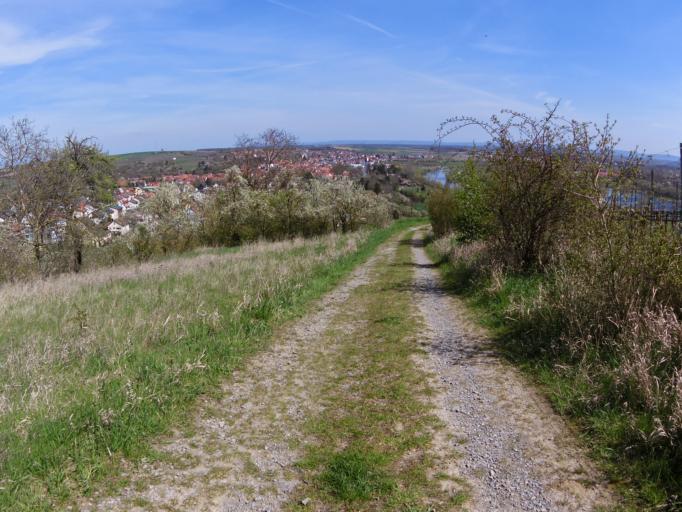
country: DE
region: Bavaria
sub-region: Regierungsbezirk Unterfranken
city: Mainstockheim
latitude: 49.7971
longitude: 10.1501
